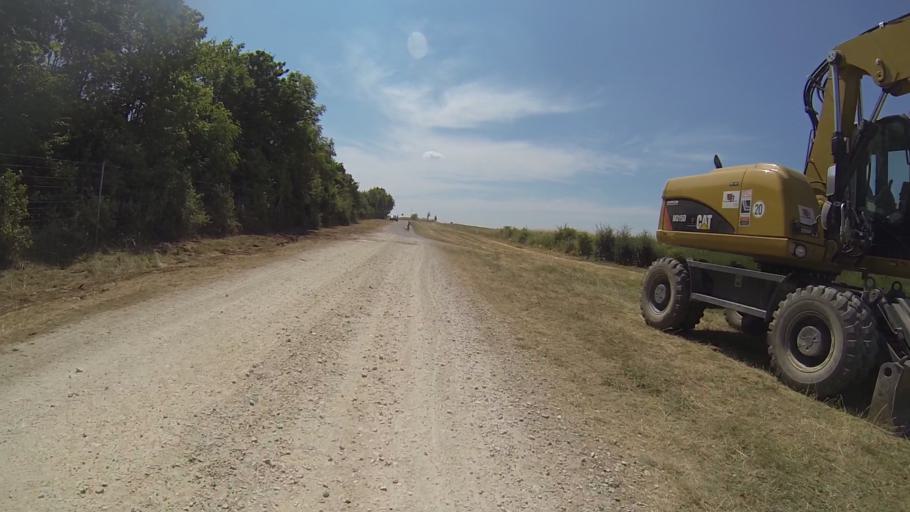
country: DE
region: Baden-Wuerttemberg
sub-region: Regierungsbezirk Stuttgart
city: Giengen an der Brenz
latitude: 48.6373
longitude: 10.2163
